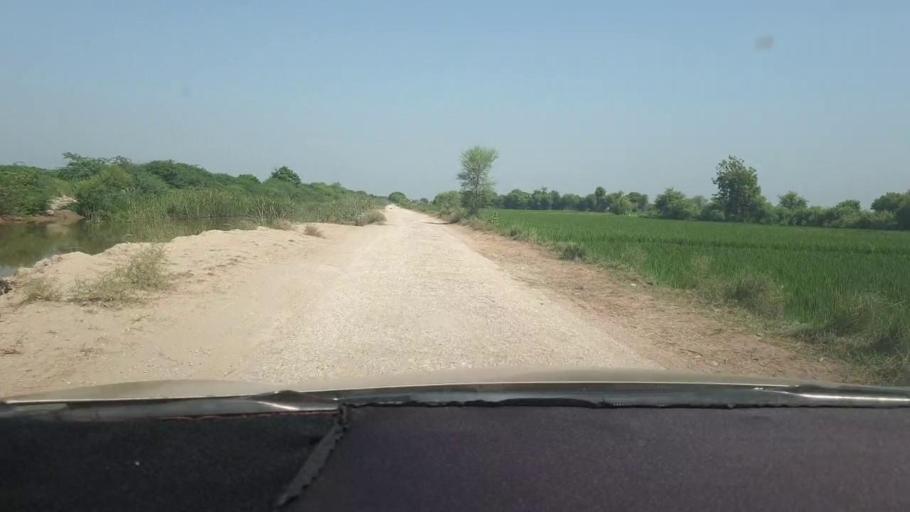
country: PK
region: Sindh
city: Miro Khan
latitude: 27.7042
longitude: 68.0809
